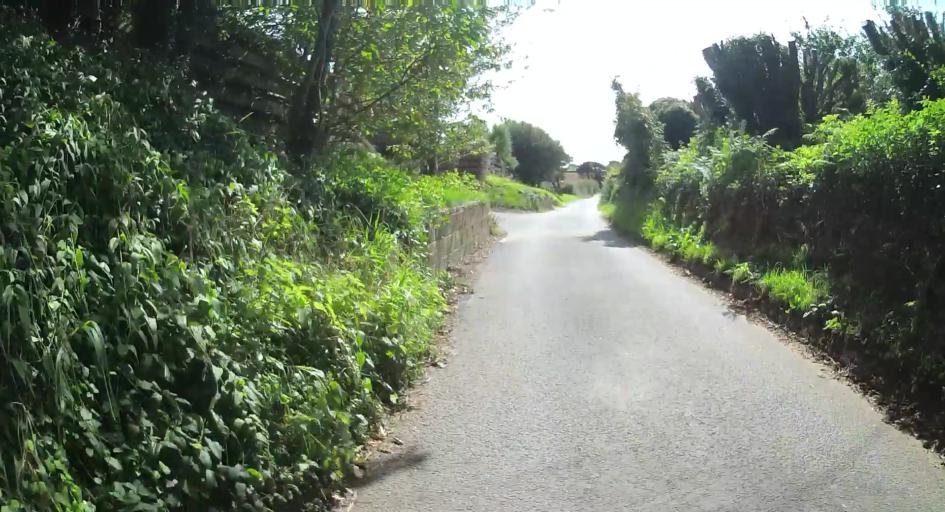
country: GB
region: England
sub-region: Isle of Wight
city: Chale
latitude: 50.6403
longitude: -1.3744
